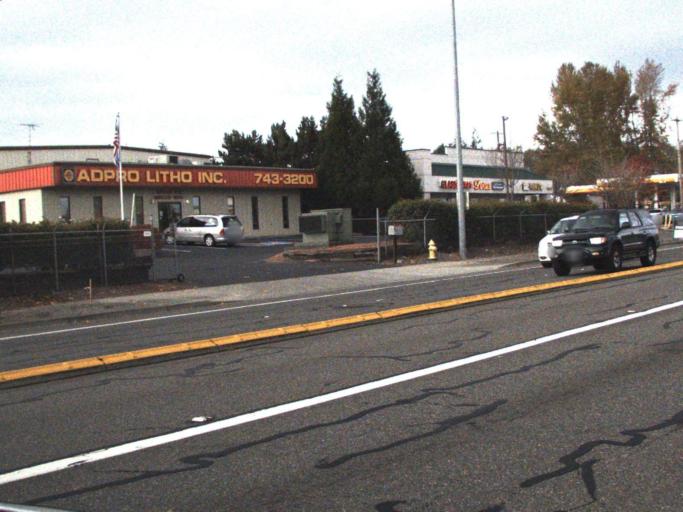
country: US
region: Washington
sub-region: Snohomish County
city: Mukilteo
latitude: 47.8982
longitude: -122.2906
